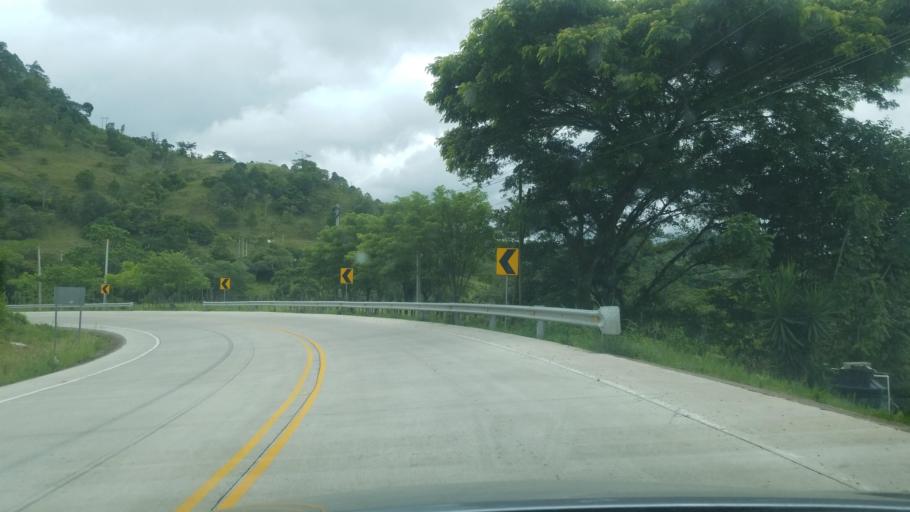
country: HN
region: Copan
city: San Jeronimo
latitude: 14.9838
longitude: -88.8692
